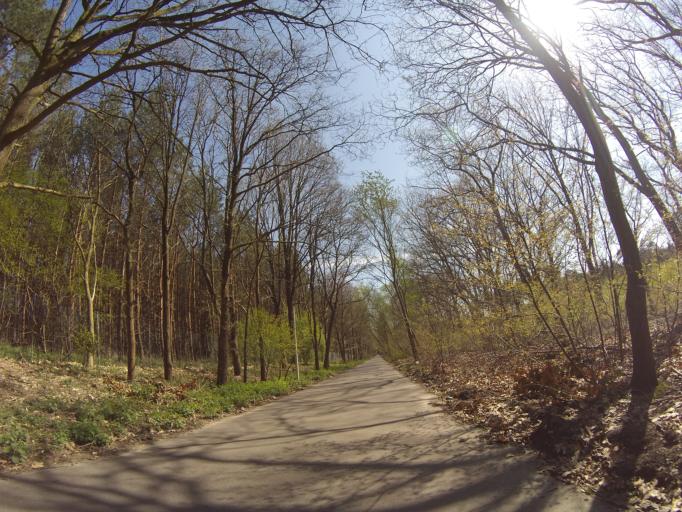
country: NL
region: Utrecht
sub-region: Gemeente Zeist
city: Zeist
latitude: 52.1108
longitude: 5.2862
